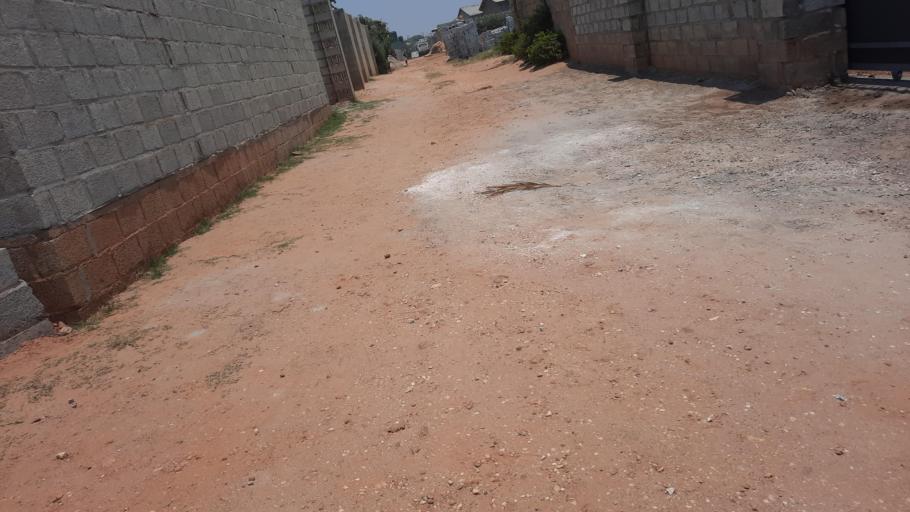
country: ZM
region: Lusaka
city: Lusaka
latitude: -15.4056
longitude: 28.3832
